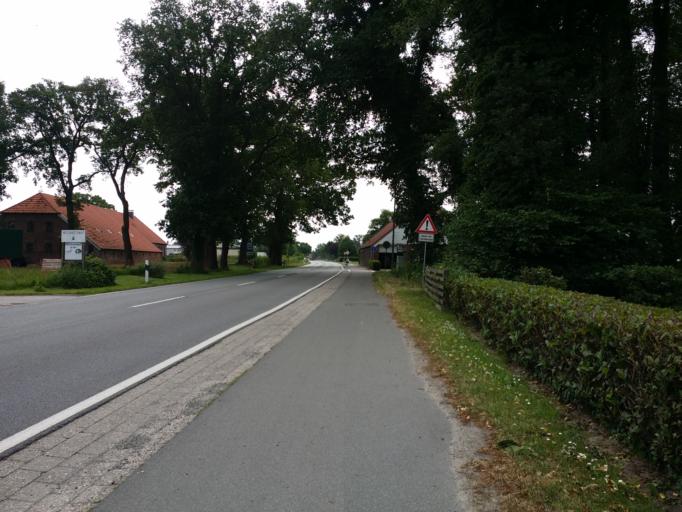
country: DE
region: Lower Saxony
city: Friedeburg
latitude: 53.4450
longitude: 7.8498
